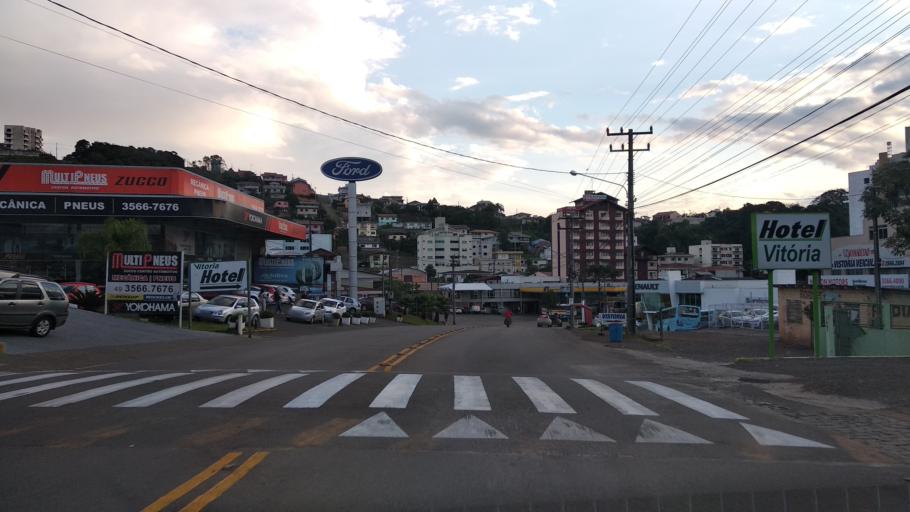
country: BR
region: Santa Catarina
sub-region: Videira
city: Videira
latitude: -27.0052
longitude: -51.1371
